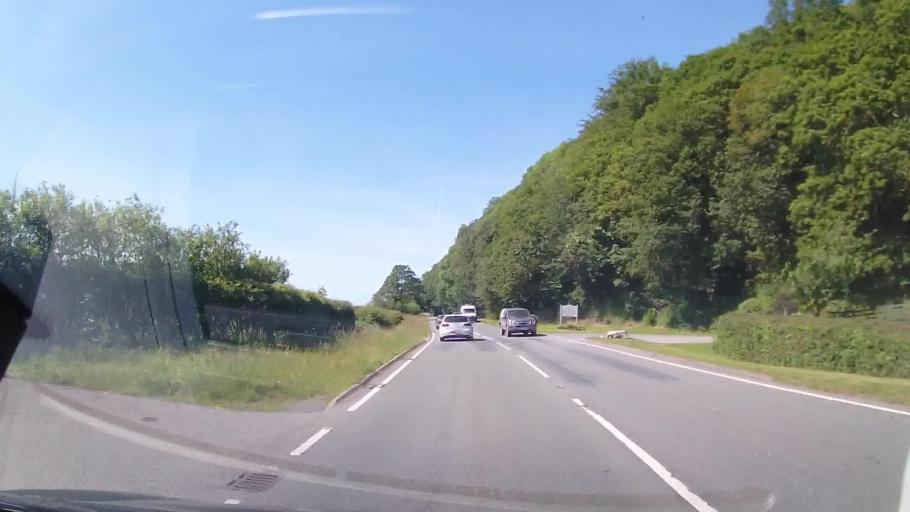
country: GB
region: Wales
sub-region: Sir Powys
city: Machynlleth
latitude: 52.5631
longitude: -3.9592
